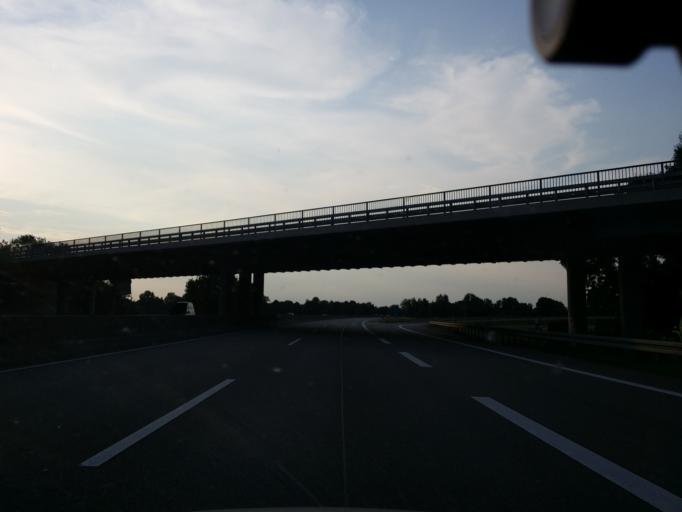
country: DE
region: Hesse
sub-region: Regierungsbezirk Darmstadt
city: Buttelborn
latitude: 49.9053
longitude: 8.5165
